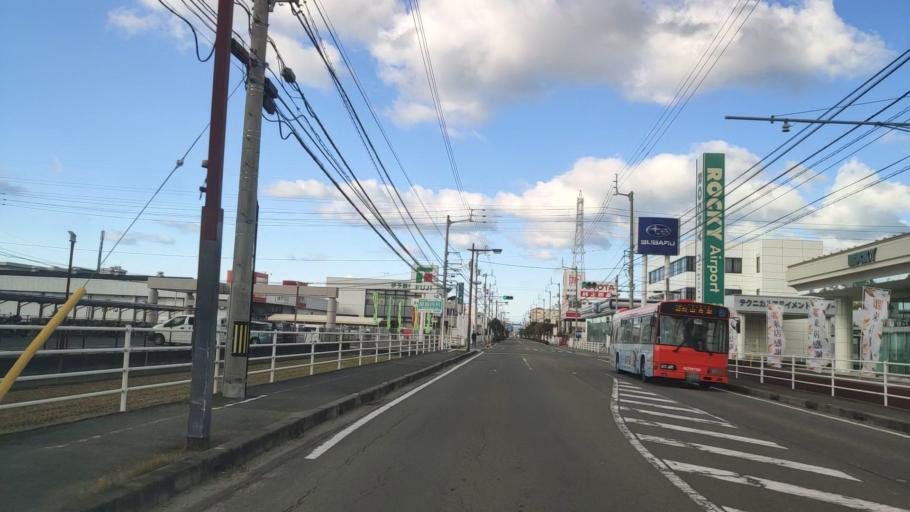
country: JP
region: Ehime
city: Masaki-cho
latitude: 33.8282
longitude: 132.7200
